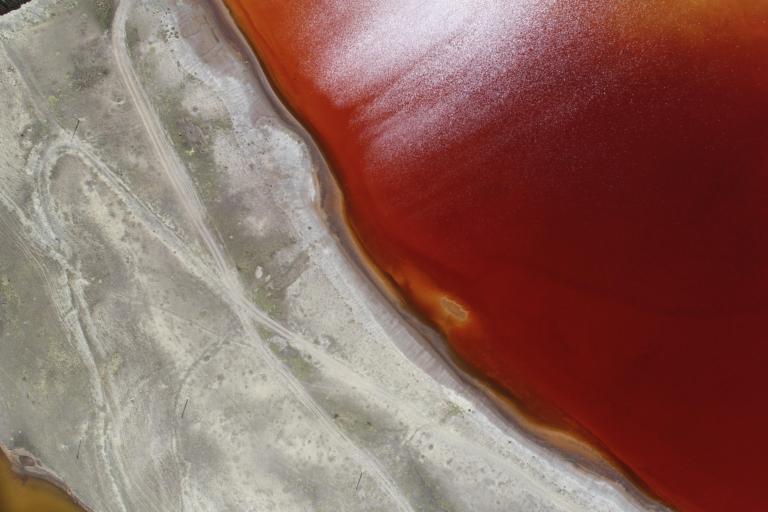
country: BO
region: La Paz
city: La Paz
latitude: -16.3430
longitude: -68.1627
